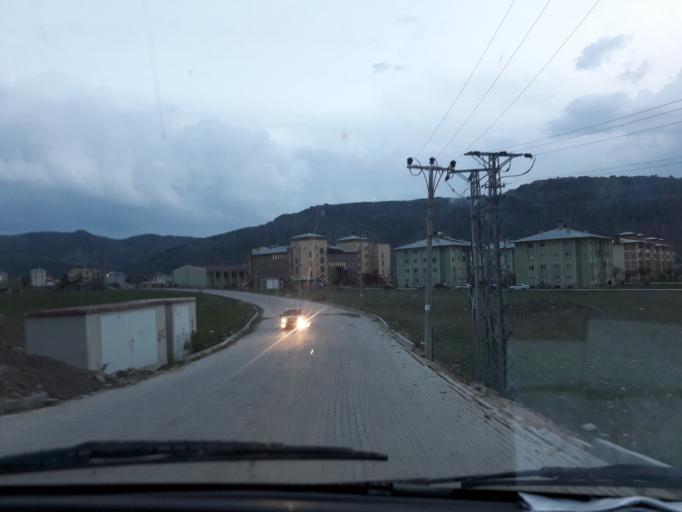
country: TR
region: Giresun
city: Alucra
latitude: 40.3255
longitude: 38.7715
